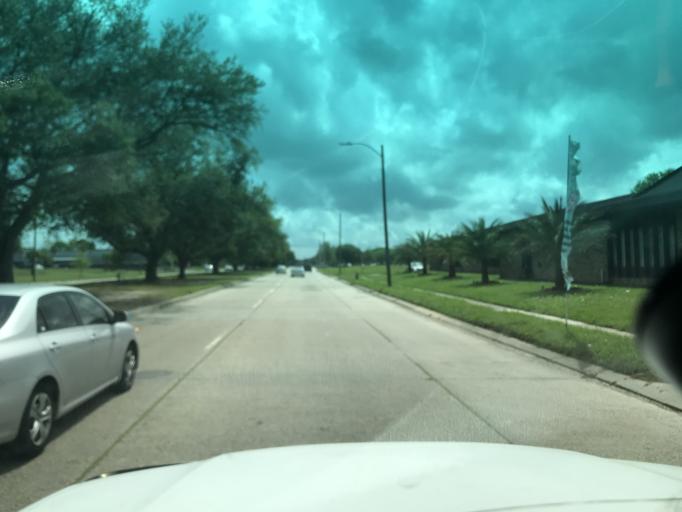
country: US
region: Louisiana
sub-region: Saint Bernard Parish
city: Chalmette
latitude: 30.0411
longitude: -89.9571
